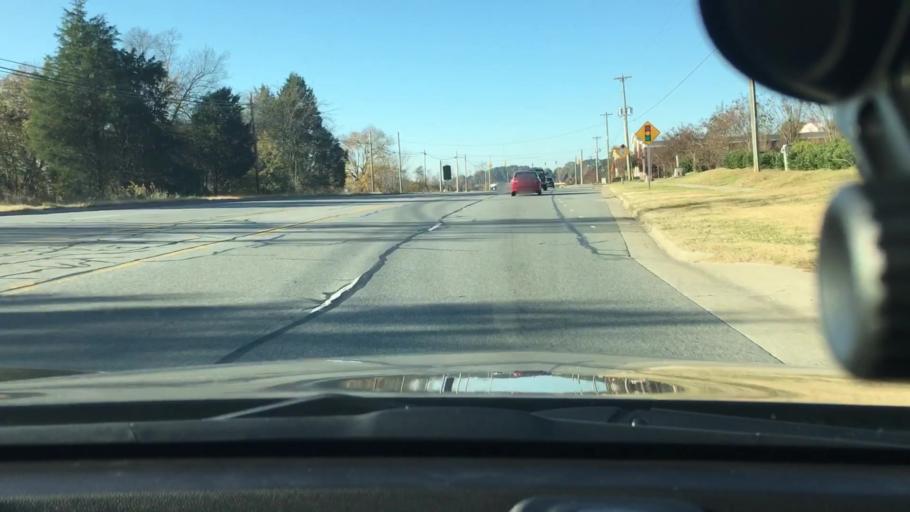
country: US
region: North Carolina
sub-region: Cabarrus County
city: Harrisburg
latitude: 35.3257
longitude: -80.6374
